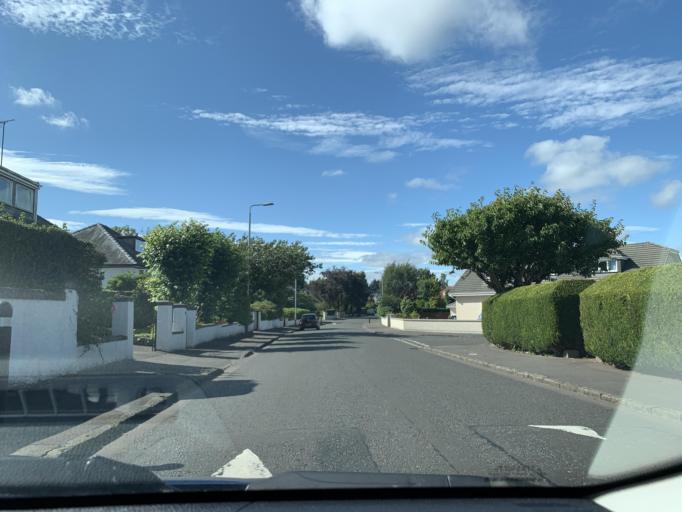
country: GB
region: Scotland
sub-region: East Renfrewshire
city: Newton Mearns
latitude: 55.7760
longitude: -4.3161
